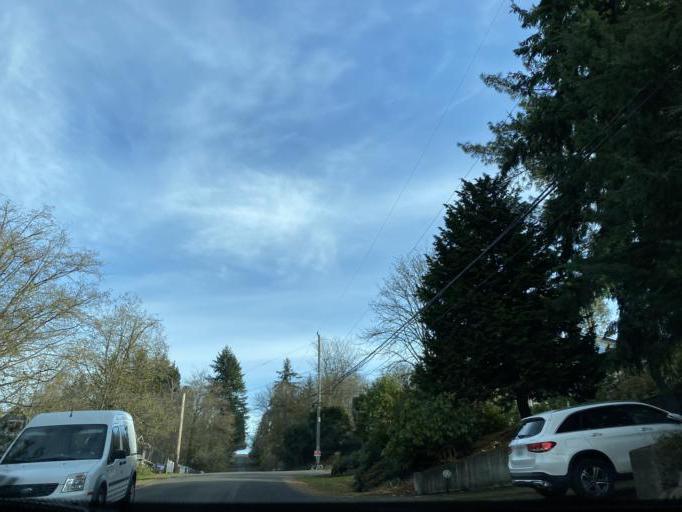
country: US
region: Washington
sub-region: King County
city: Lake Forest Park
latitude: 47.7003
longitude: -122.2996
